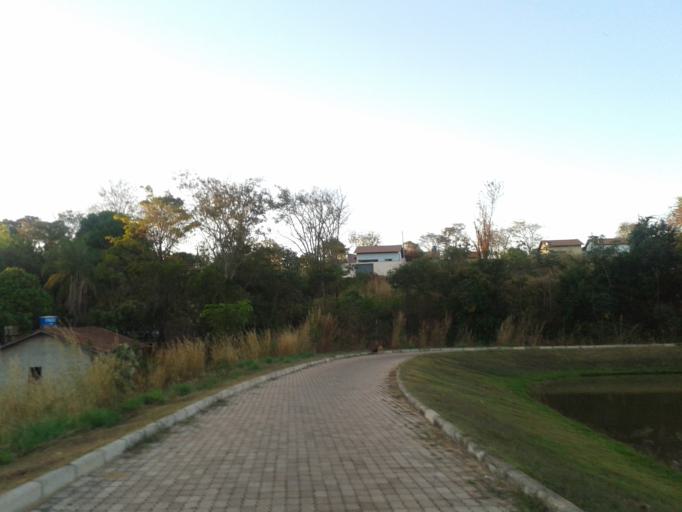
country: BR
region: Goias
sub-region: Sao Miguel Do Araguaia
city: Sao Miguel do Araguaia
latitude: -13.2687
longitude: -50.1669
